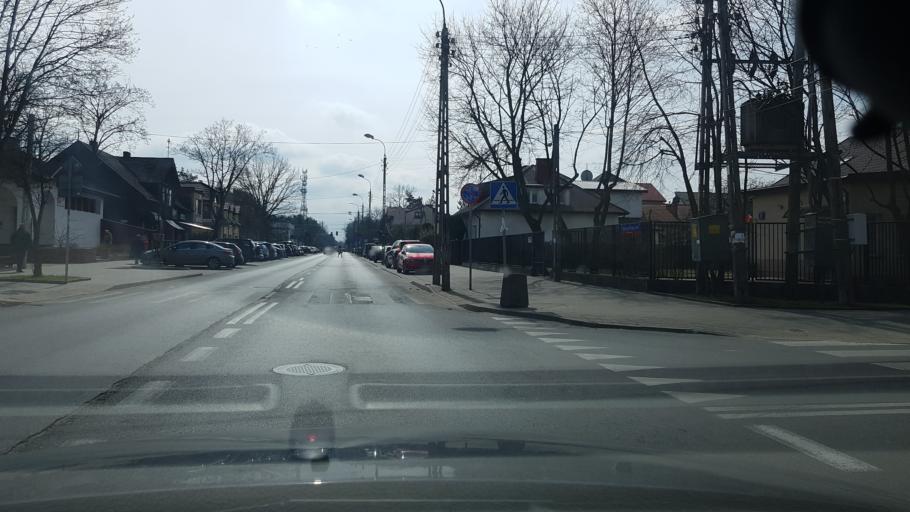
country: PL
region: Masovian Voivodeship
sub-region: Warszawa
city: Wesola
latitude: 52.2528
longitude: 21.2240
